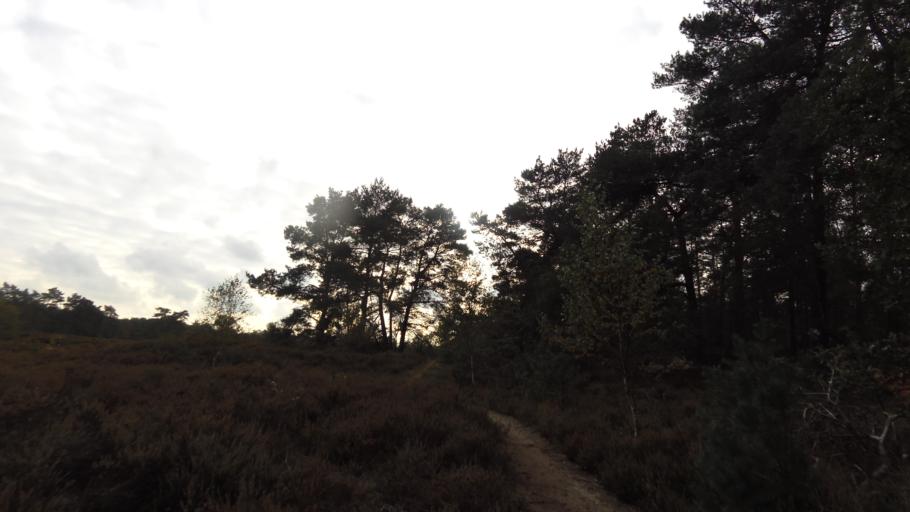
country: NL
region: Gelderland
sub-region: Gemeente Epe
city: Emst
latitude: 52.3241
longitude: 5.9064
